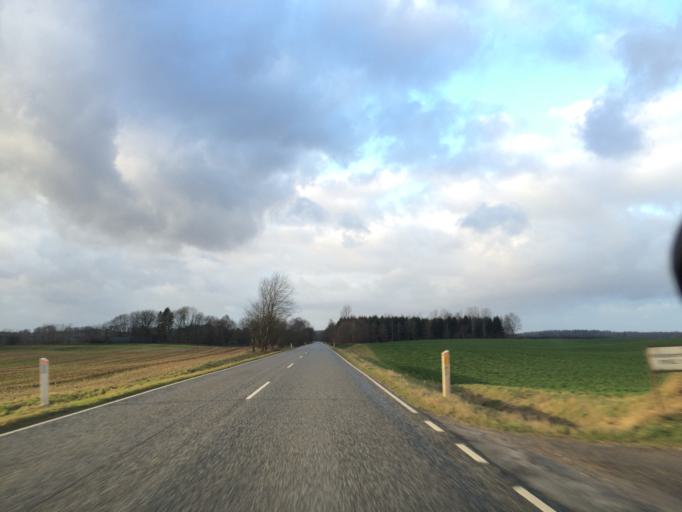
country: DK
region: Central Jutland
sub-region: Silkeborg Kommune
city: Svejbaek
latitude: 56.1015
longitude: 9.6000
